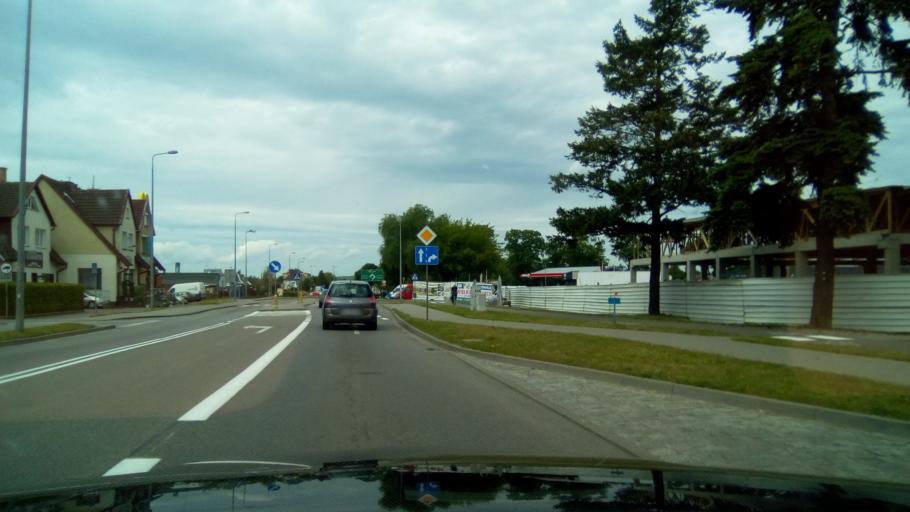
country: PL
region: Pomeranian Voivodeship
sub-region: Powiat leborski
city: Lebork
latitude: 54.5312
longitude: 17.7612
